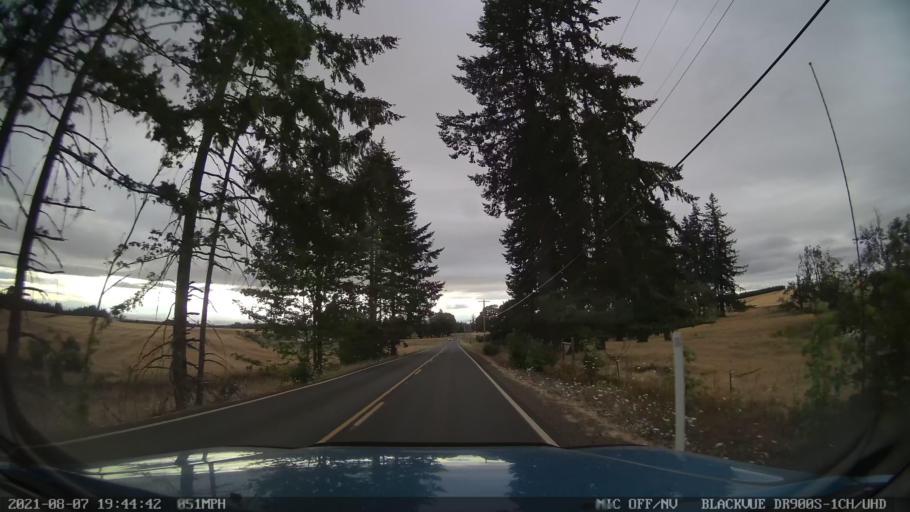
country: US
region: Oregon
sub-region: Marion County
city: Silverton
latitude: 44.9417
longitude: -122.6866
